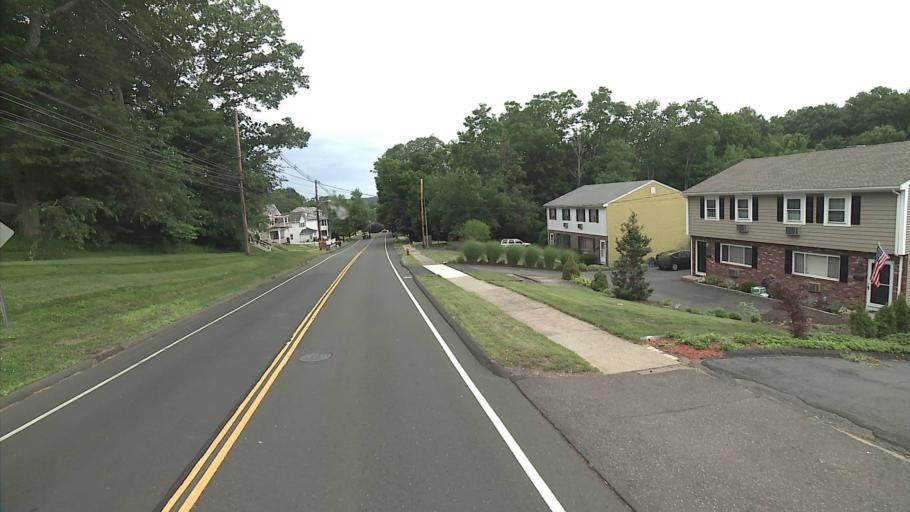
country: US
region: Connecticut
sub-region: New Haven County
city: Wallingford Center
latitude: 41.4484
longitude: -72.8058
